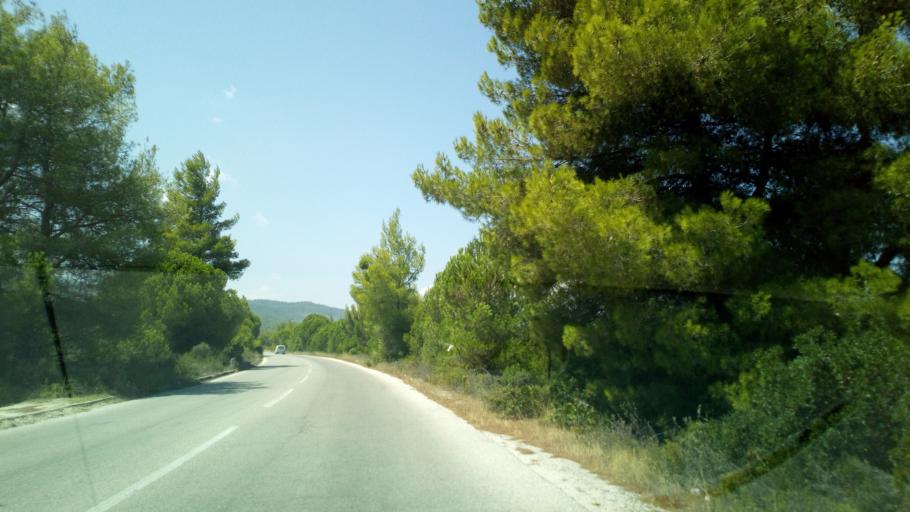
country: GR
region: Central Macedonia
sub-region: Nomos Chalkidikis
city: Sarti
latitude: 40.1279
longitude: 23.9432
